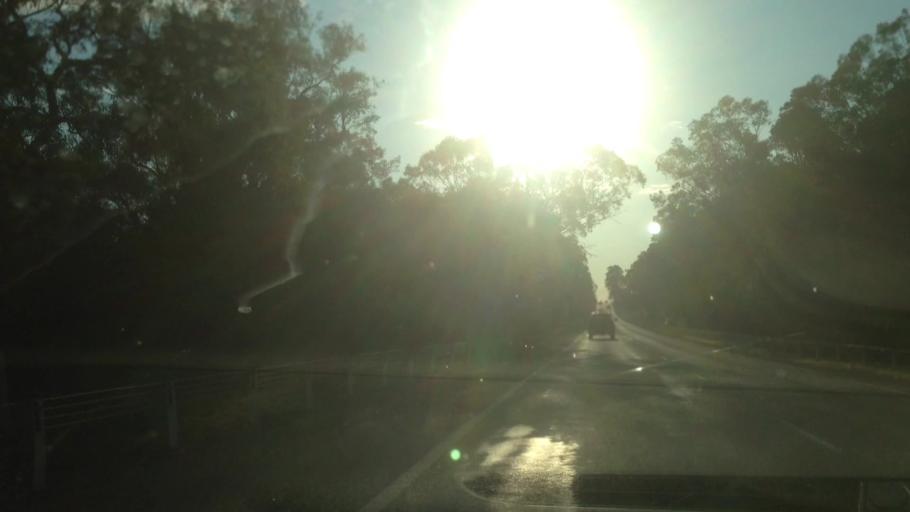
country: AU
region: New South Wales
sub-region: Cessnock
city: Kurri Kurri
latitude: -32.8290
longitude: 151.4977
